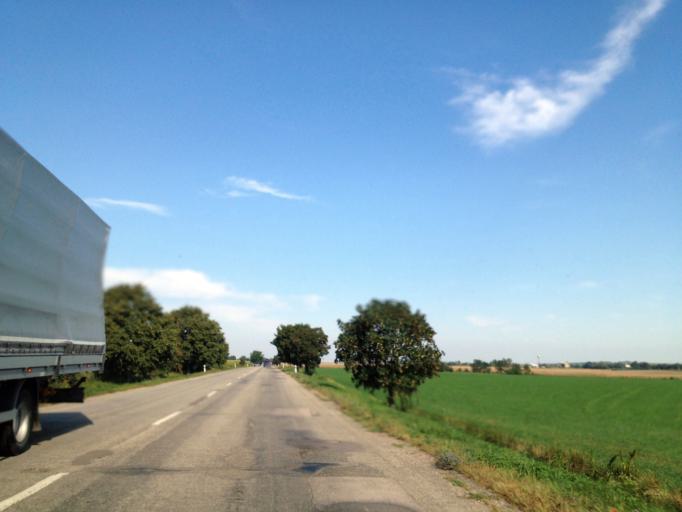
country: SK
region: Nitriansky
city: Svodin
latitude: 47.8877
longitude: 18.4117
